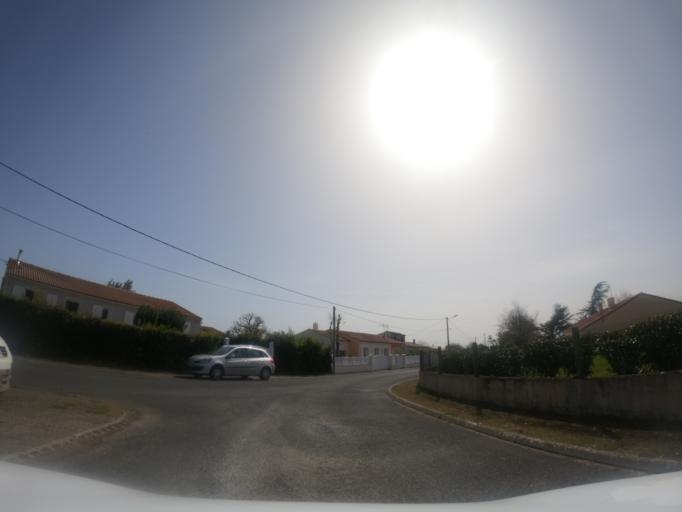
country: FR
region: Pays de la Loire
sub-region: Departement de la Vendee
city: Vix
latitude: 46.3951
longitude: -0.8133
